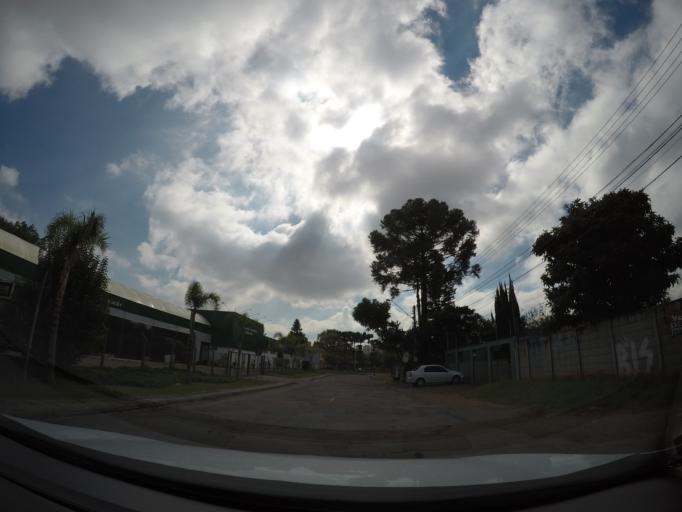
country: BR
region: Parana
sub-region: Sao Jose Dos Pinhais
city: Sao Jose dos Pinhais
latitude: -25.4917
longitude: -49.2230
